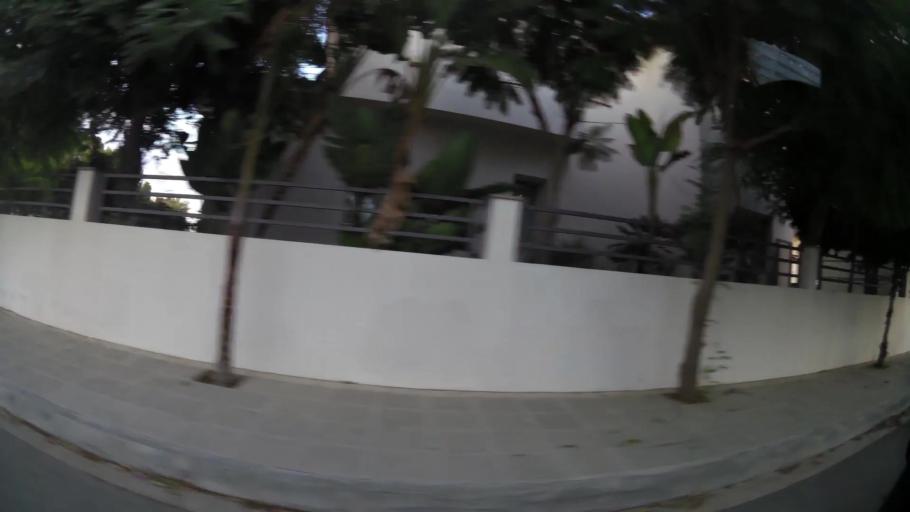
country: CY
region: Lefkosia
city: Nicosia
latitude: 35.1580
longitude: 33.3277
